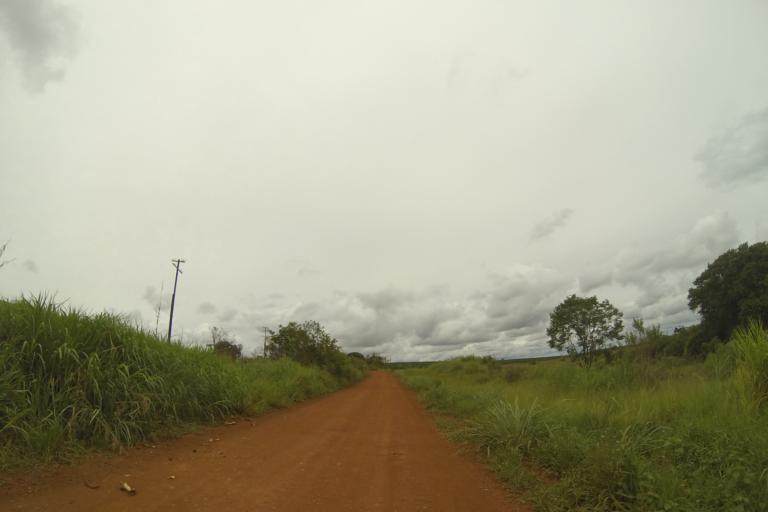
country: BR
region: Minas Gerais
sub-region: Ibia
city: Ibia
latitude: -19.6145
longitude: -46.6676
